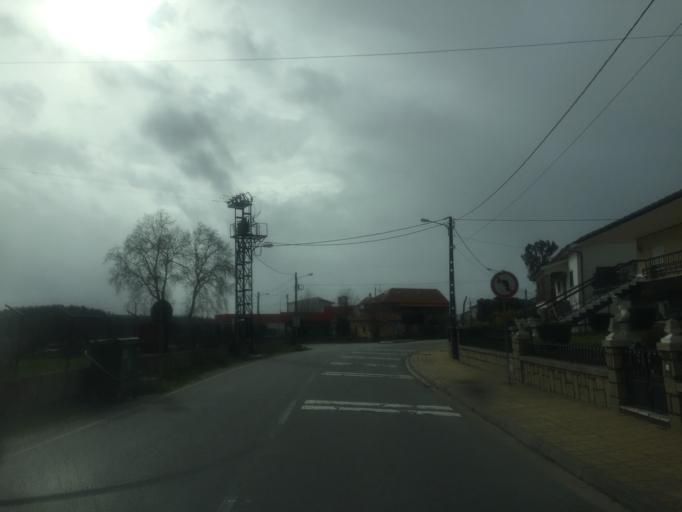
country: PT
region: Guarda
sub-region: Seia
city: Seia
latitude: 40.4023
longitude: -7.7415
